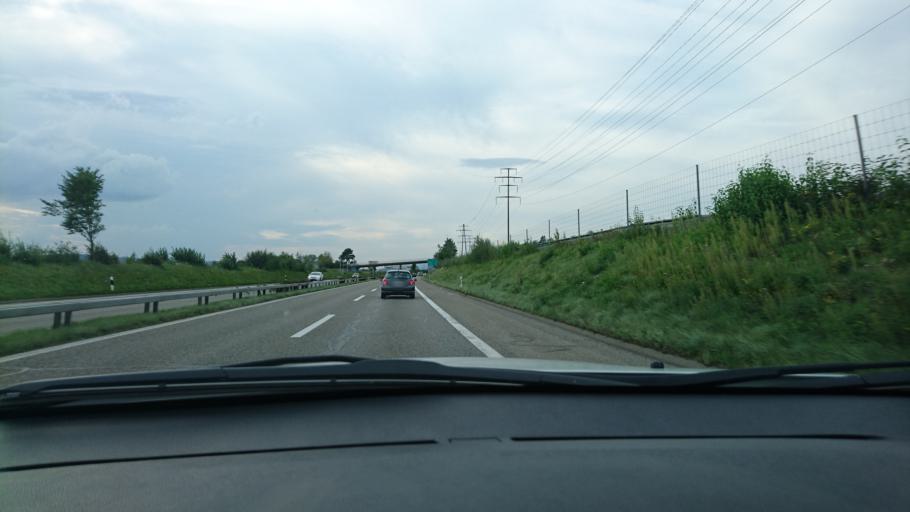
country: CH
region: Zurich
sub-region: Bezirk Uster
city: Naenikon / Naenikon (Dorfkern)
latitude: 47.3733
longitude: 8.7006
